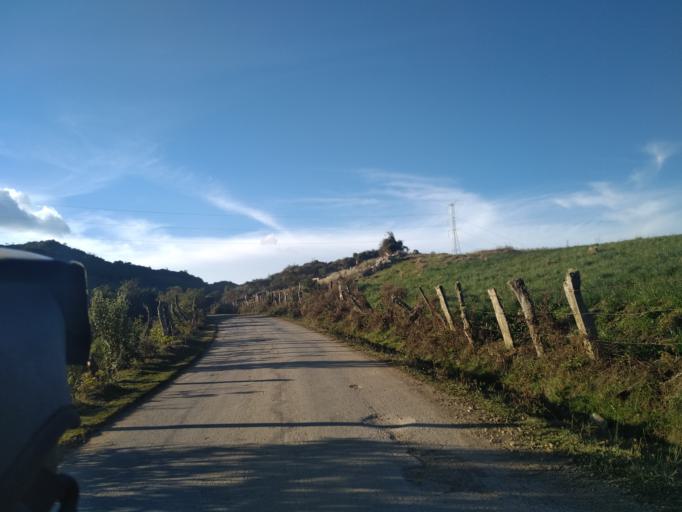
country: PE
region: Amazonas
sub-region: Provincia de Chachapoyas
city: Montevideo
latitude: -6.7169
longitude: -77.8656
